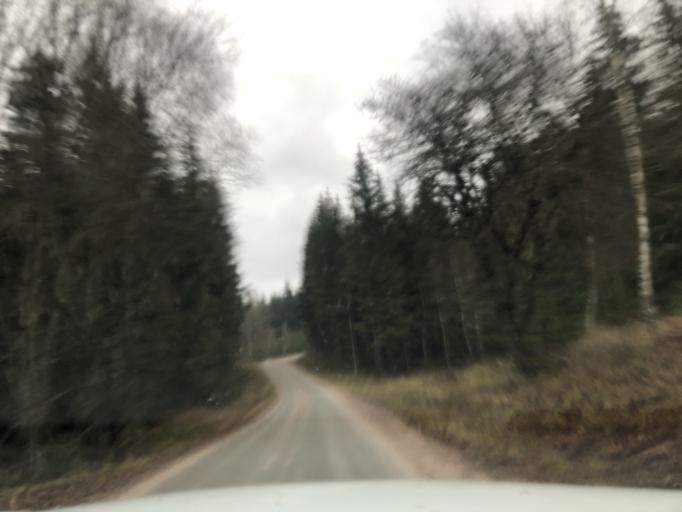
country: SE
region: Vaestra Goetaland
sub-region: Ulricehamns Kommun
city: Ulricehamn
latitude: 57.8730
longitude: 13.5602
